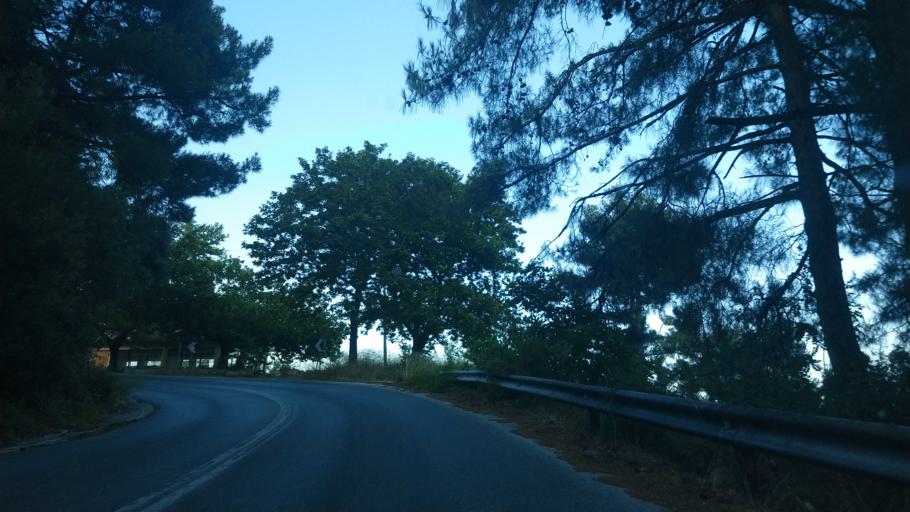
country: GR
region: East Macedonia and Thrace
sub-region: Nomos Kavalas
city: Potamia
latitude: 40.7209
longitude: 24.7348
